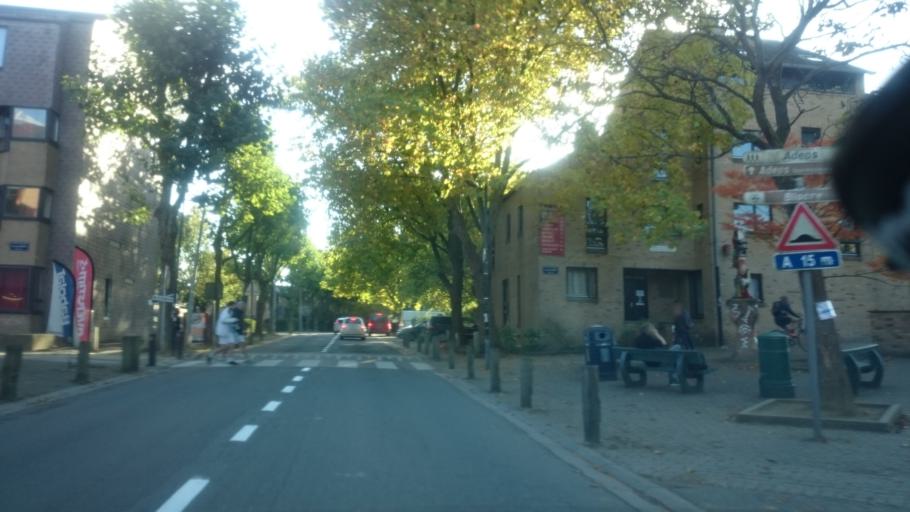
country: BE
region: Wallonia
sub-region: Province du Brabant Wallon
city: Louvain-la-Neuve
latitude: 50.6703
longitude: 4.6032
